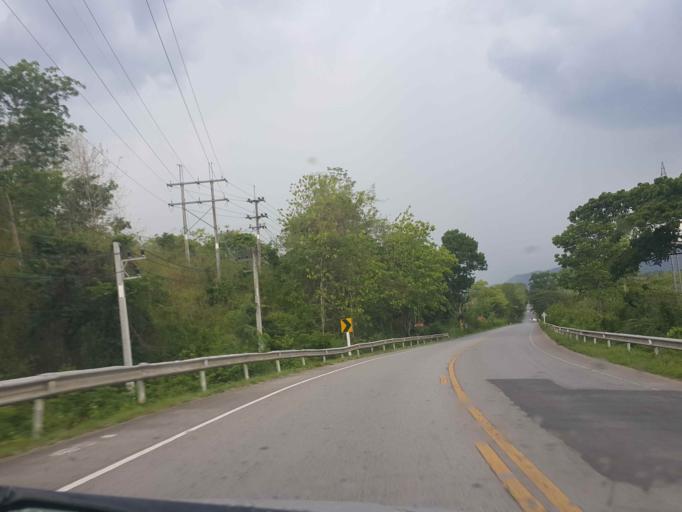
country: TH
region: Phrae
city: Den Chai
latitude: 17.9660
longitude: 100.0523
